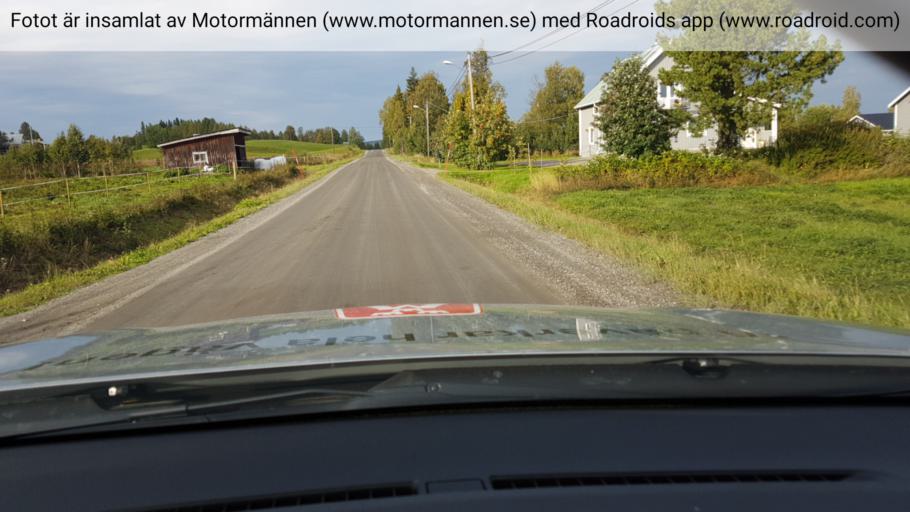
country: SE
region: Jaemtland
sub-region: Stroemsunds Kommun
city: Stroemsund
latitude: 64.0475
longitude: 15.8107
